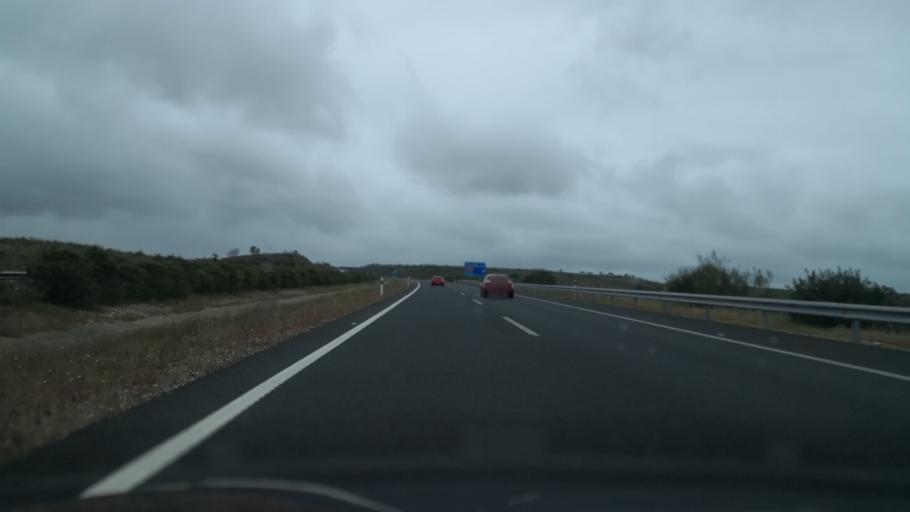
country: ES
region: Extremadura
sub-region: Provincia de Caceres
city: Hinojal
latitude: 39.7120
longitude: -6.4092
